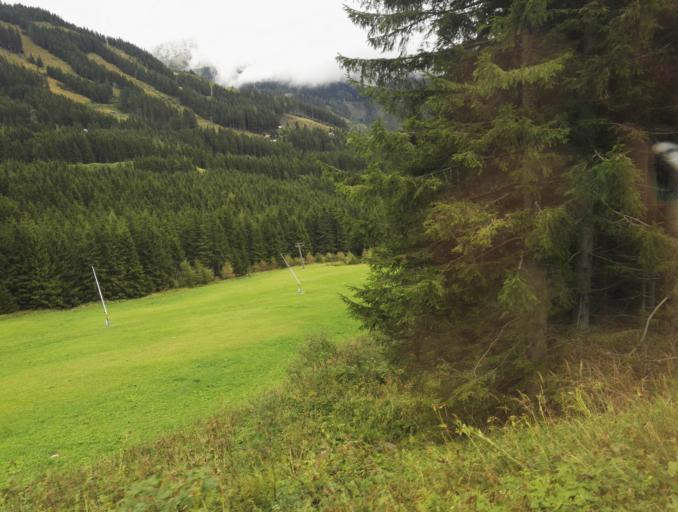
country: AT
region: Styria
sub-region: Politischer Bezirk Leoben
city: Vordernberg
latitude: 47.5181
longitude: 14.9528
